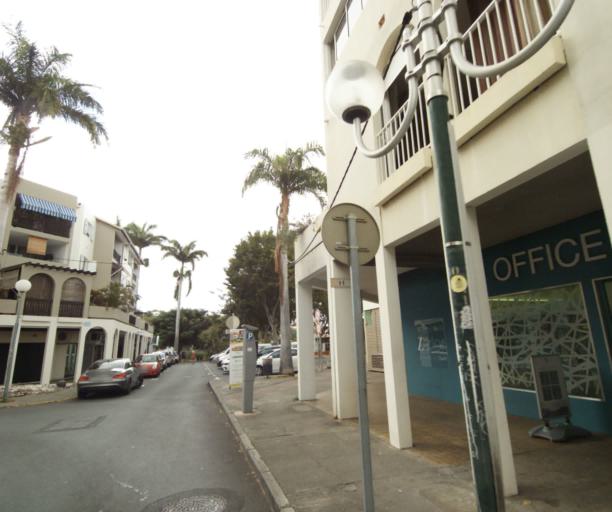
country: RE
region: Reunion
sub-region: Reunion
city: Saint-Paul
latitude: -21.0523
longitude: 55.2261
